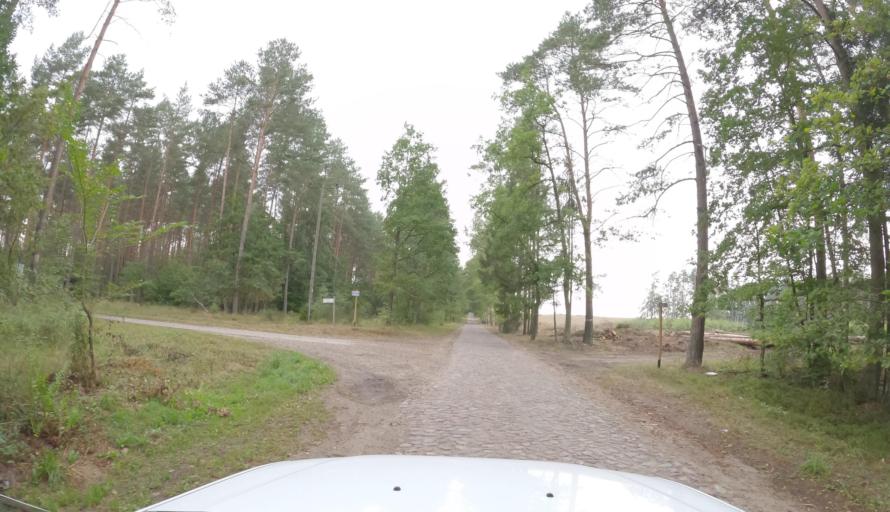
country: PL
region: West Pomeranian Voivodeship
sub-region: Powiat kolobrzeski
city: Ryman
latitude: 53.8591
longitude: 15.5766
